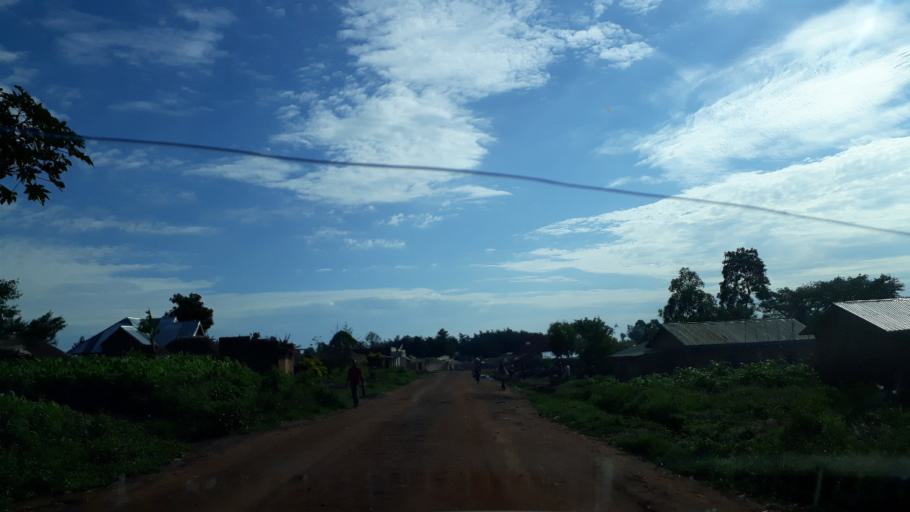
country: UG
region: Northern Region
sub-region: Zombo District
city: Paidha
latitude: 2.3068
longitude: 31.0183
